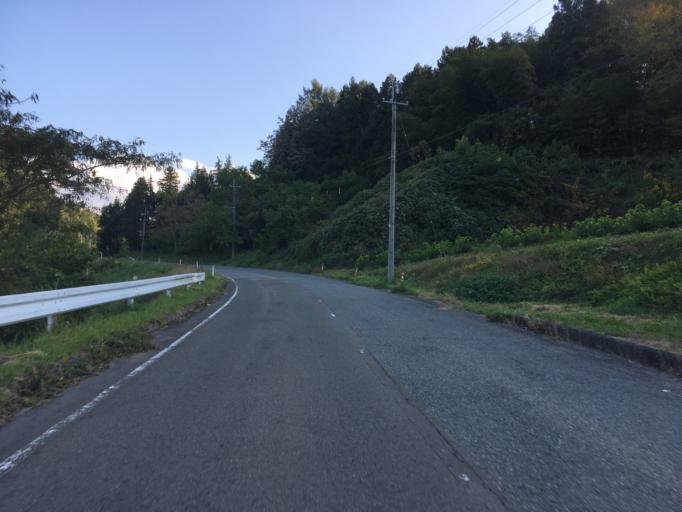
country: JP
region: Fukushima
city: Nihommatsu
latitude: 37.6408
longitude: 140.5532
